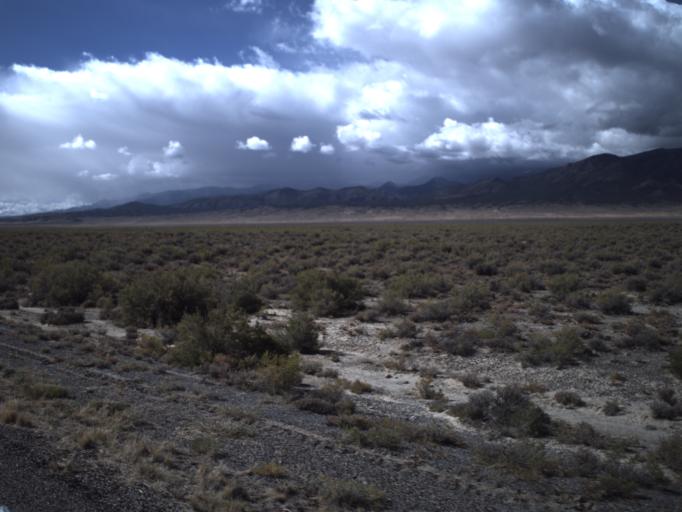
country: US
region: Nevada
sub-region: White Pine County
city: McGill
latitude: 39.0147
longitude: -114.0353
